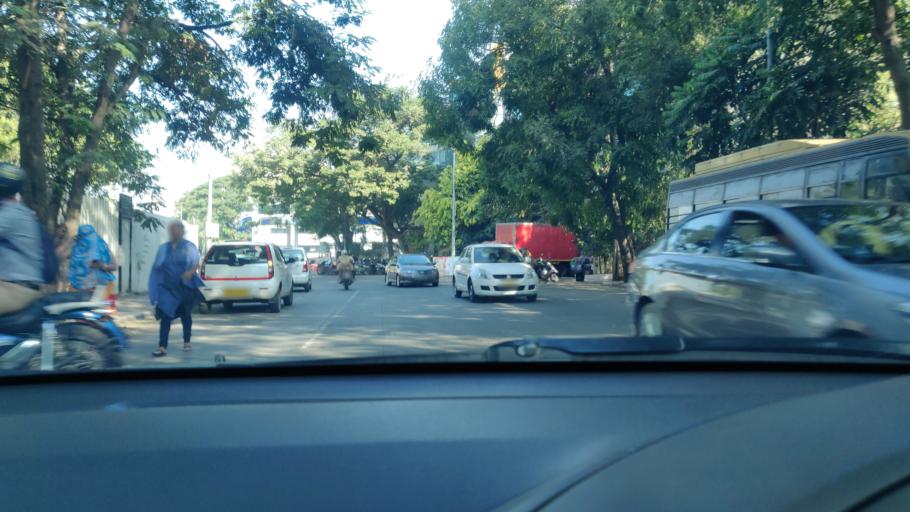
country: IN
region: Maharashtra
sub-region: Pune Division
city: Khadki
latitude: 18.5570
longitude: 73.8044
